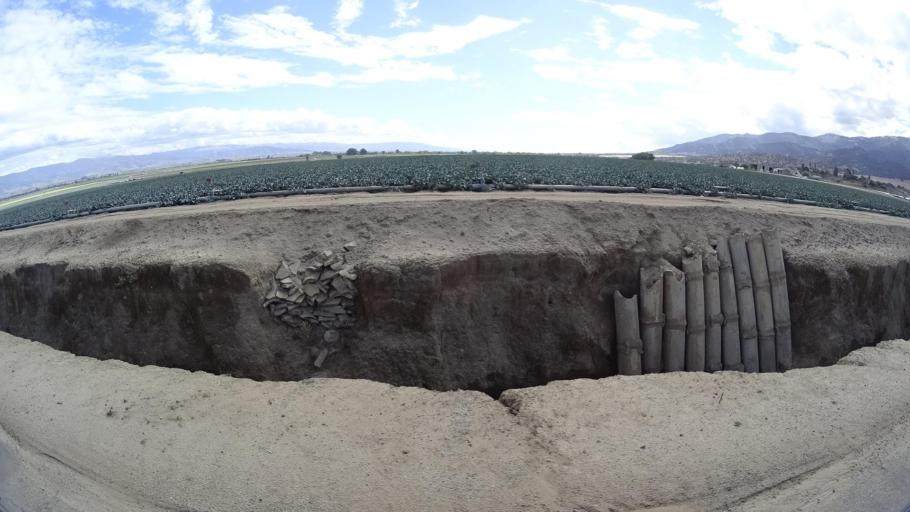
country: US
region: California
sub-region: Monterey County
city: Chualar
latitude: 36.5924
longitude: -121.6048
